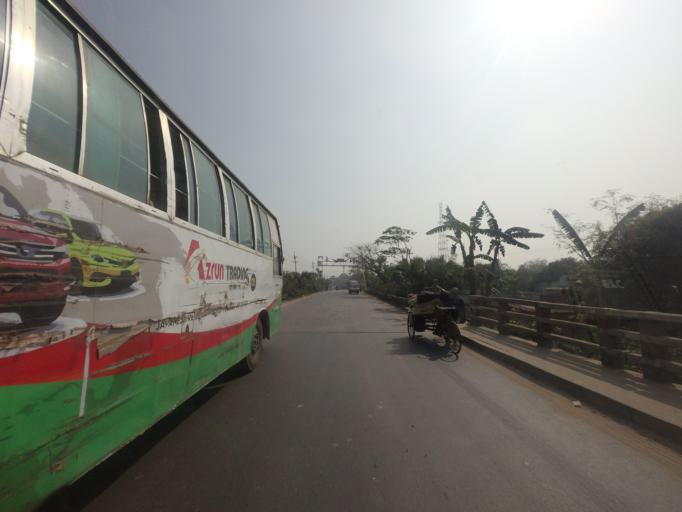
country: BD
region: Dhaka
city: Narsingdi
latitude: 23.8936
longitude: 90.6671
